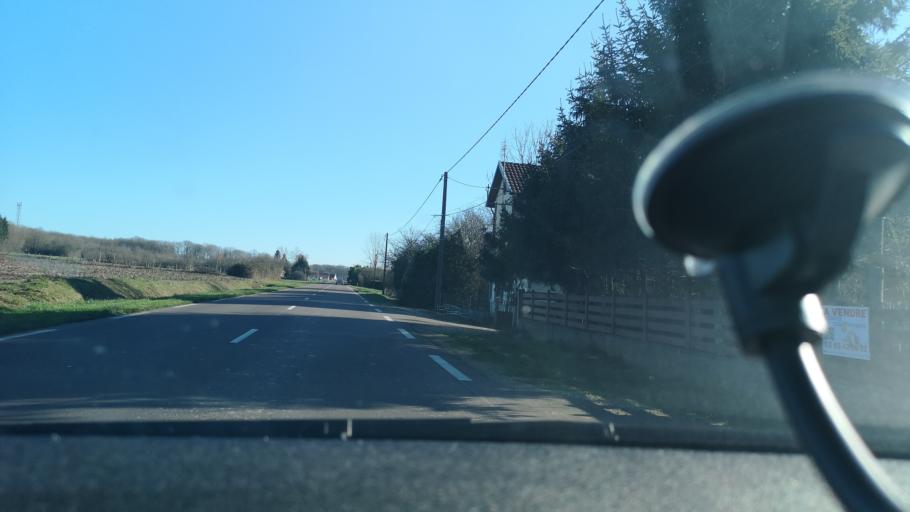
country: FR
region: Bourgogne
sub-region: Departement de Saone-et-Loire
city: Ouroux-sur-Saone
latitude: 46.7722
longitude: 4.9703
